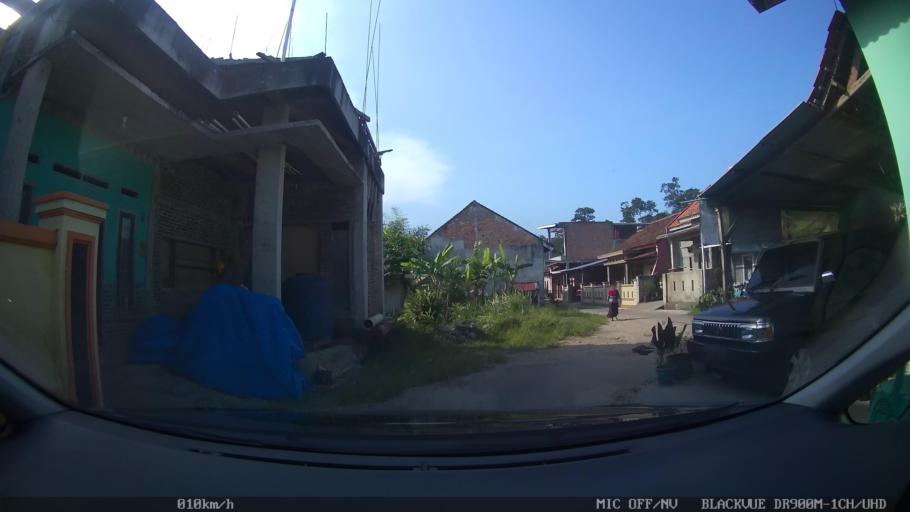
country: ID
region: Lampung
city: Kedaton
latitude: -5.3792
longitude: 105.2321
